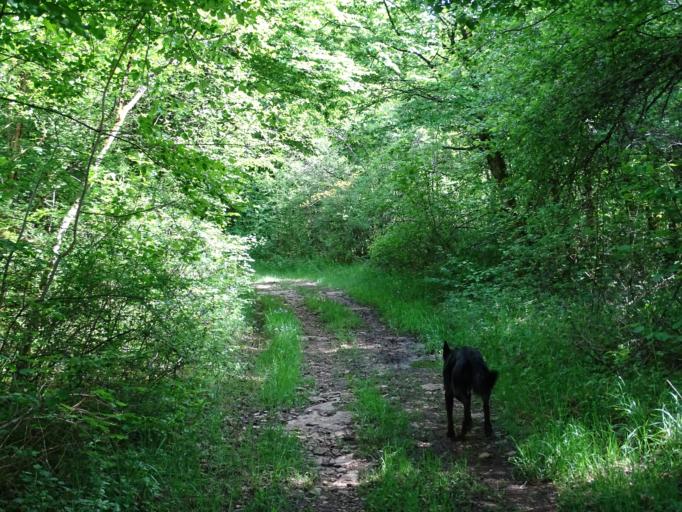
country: FR
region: Franche-Comte
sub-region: Departement du Doubs
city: Levier
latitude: 47.0190
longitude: 5.9996
